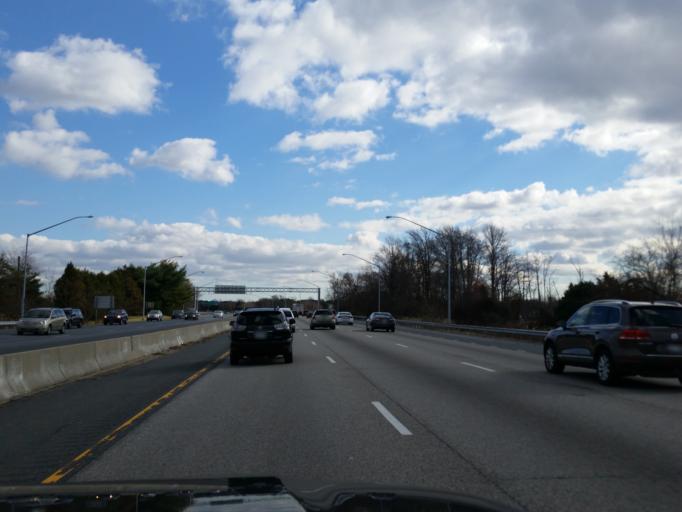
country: US
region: Maryland
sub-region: Queen Anne's County
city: Stevensville
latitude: 38.9759
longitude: -76.3082
